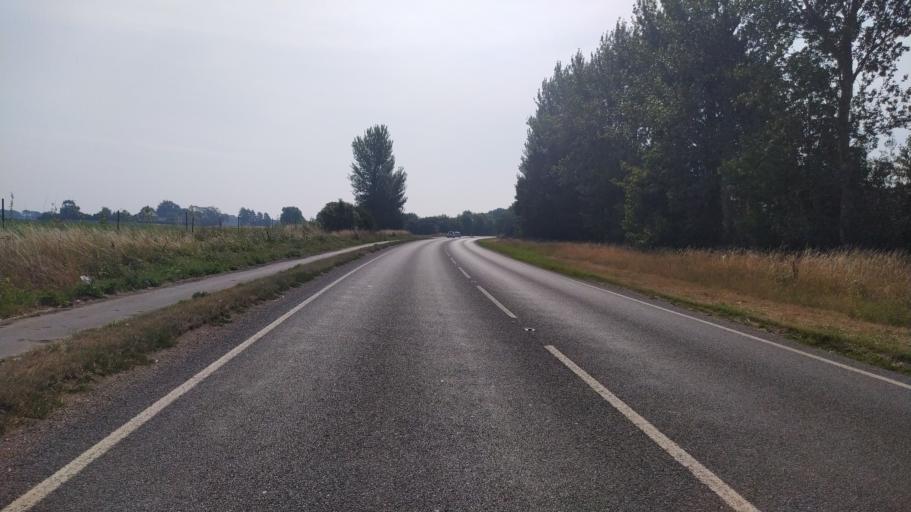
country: GB
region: England
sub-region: West Sussex
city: Boxgrove
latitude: 50.8216
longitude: -0.7203
